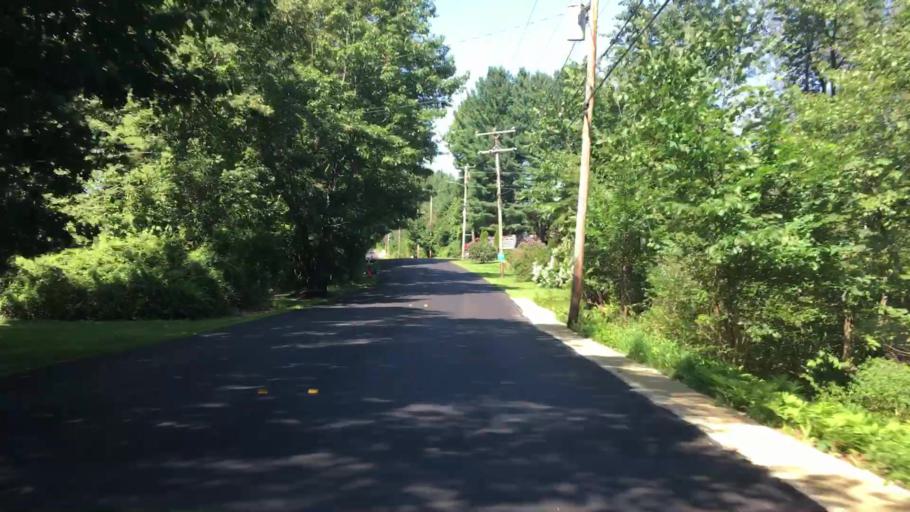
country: US
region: Maine
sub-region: York County
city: Eliot
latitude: 43.1691
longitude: -70.8400
